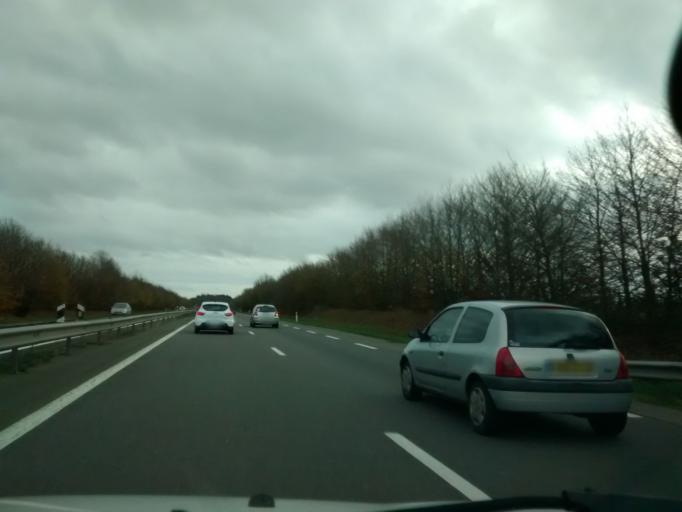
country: FR
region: Brittany
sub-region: Departement d'Ille-et-Vilaine
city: Saint-Domineuc
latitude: 48.3566
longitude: -1.8684
